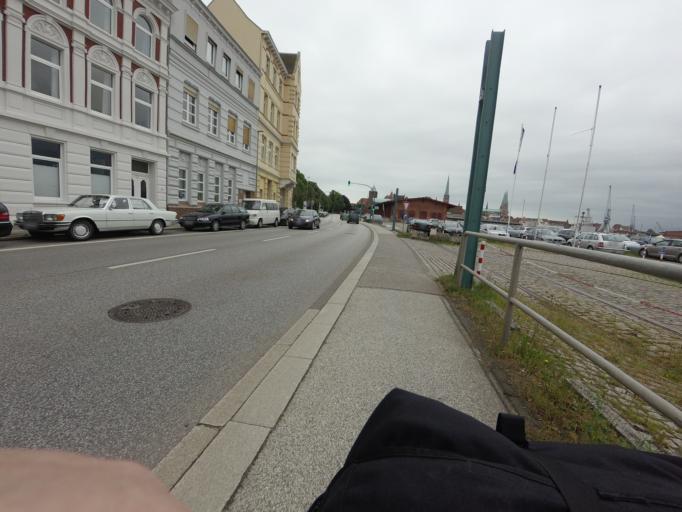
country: DE
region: Schleswig-Holstein
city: Luebeck
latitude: 53.8777
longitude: 10.6909
